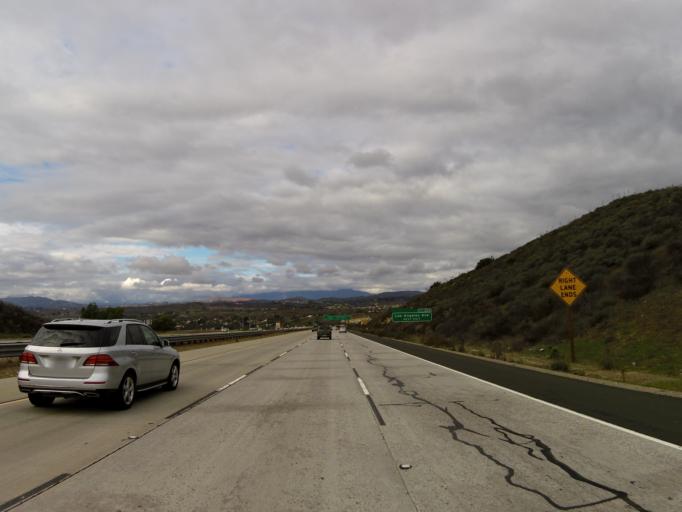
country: US
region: California
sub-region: Ventura County
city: Moorpark
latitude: 34.2759
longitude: -118.8583
